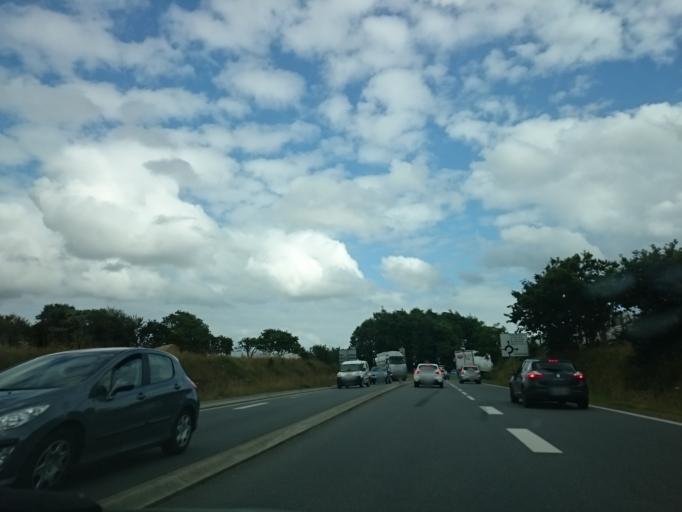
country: FR
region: Brittany
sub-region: Departement du Finistere
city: Gouesnou
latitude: 48.4320
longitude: -4.4413
